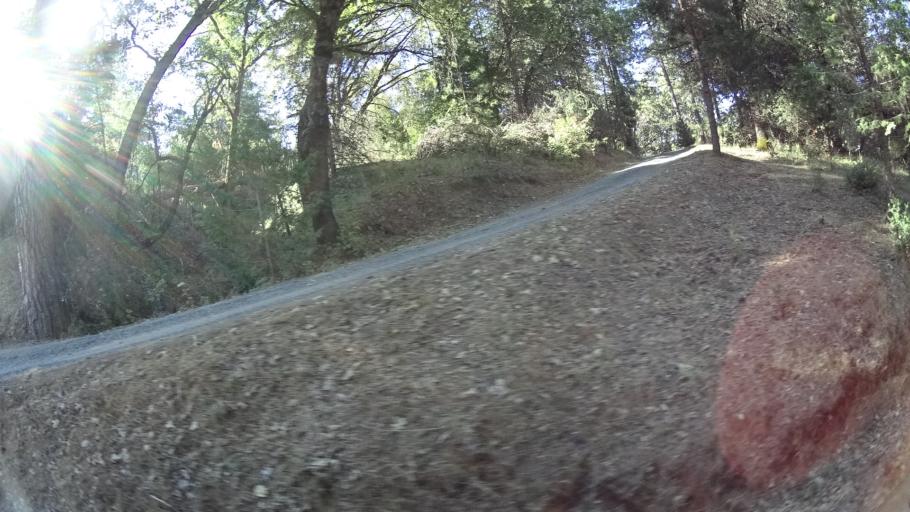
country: US
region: California
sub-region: Amador County
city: Pioneer
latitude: 38.3850
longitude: -120.5606
